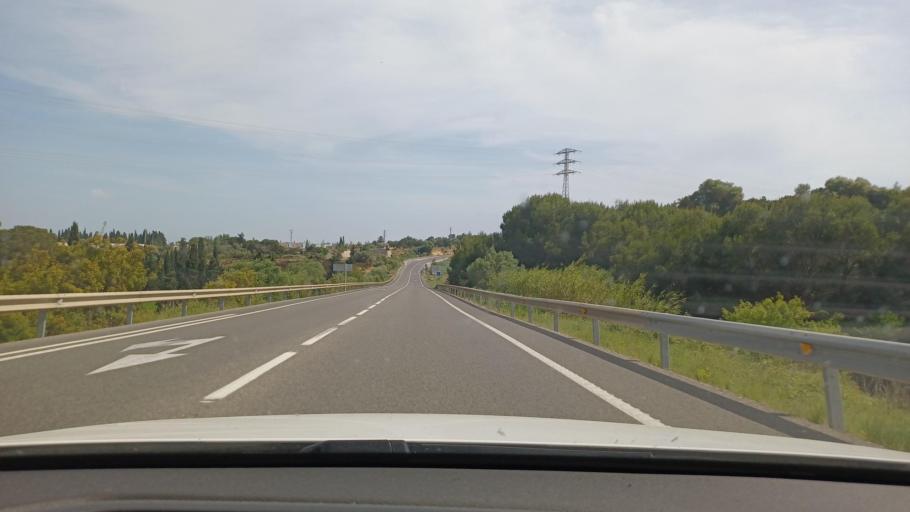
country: ES
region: Catalonia
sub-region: Provincia de Tarragona
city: Amposta
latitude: 40.7142
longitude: 0.5641
